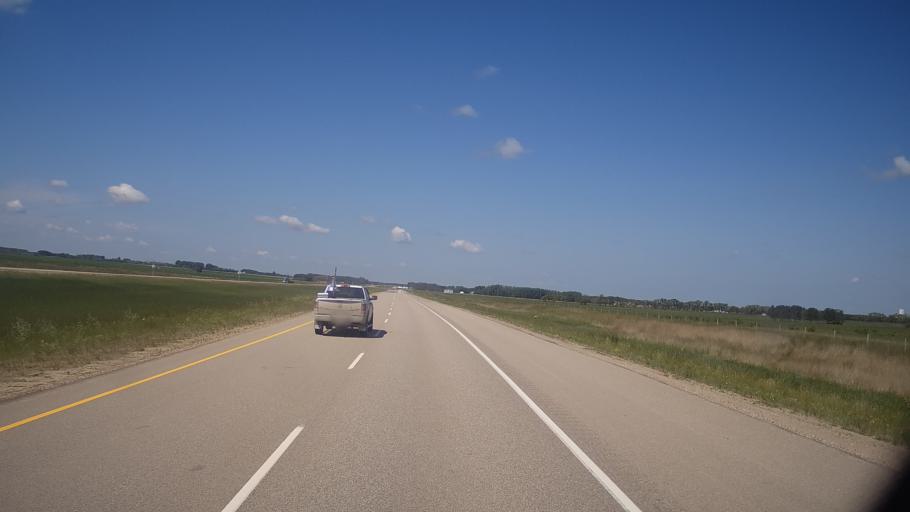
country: CA
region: Saskatchewan
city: Saskatoon
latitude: 52.0123
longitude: -106.3675
